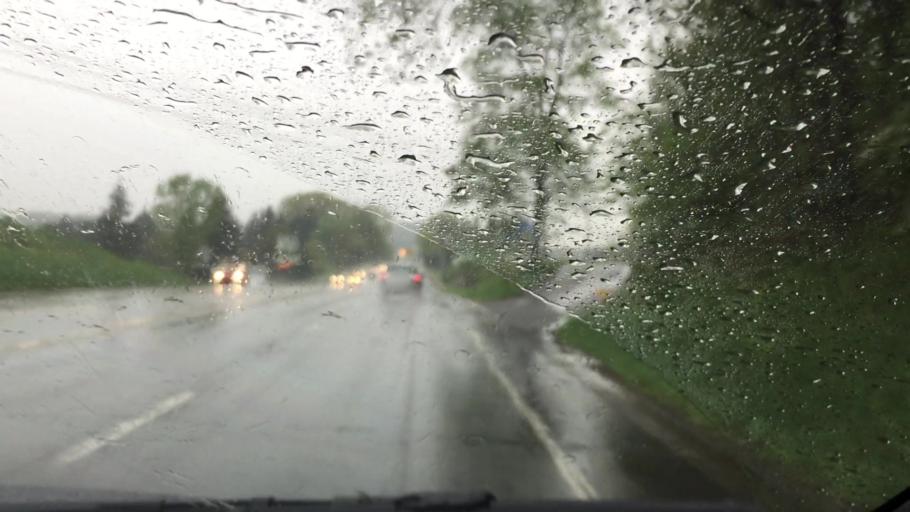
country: US
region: Pennsylvania
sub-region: Butler County
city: Nixon
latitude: 40.7507
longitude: -79.9248
